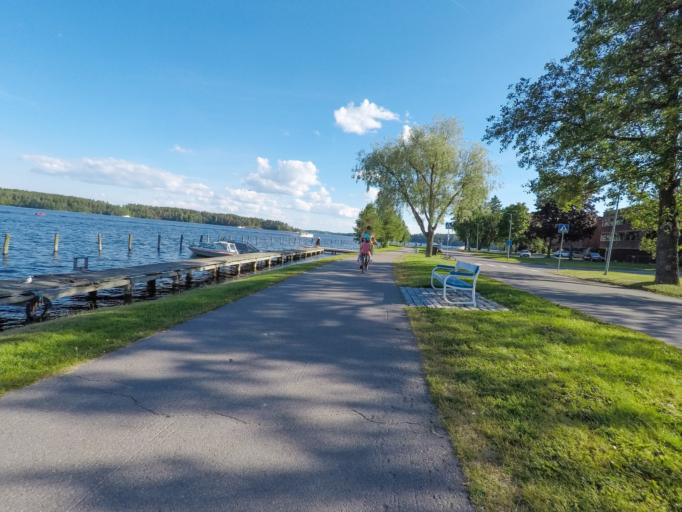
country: FI
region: Southern Savonia
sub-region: Savonlinna
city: Savonlinna
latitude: 61.8651
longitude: 28.8670
